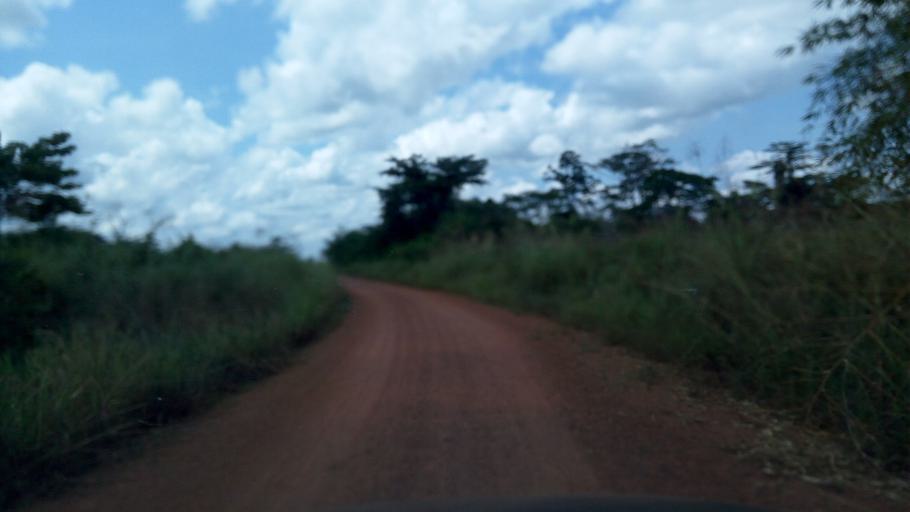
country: CD
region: Equateur
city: Libenge
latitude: 3.9896
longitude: 18.7254
